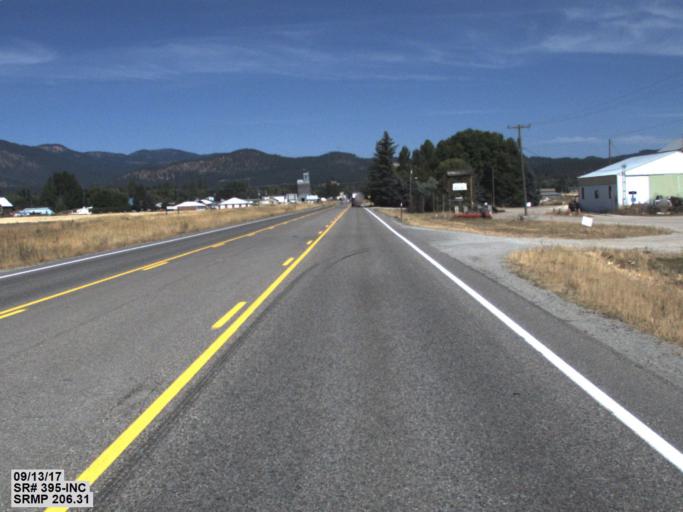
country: US
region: Washington
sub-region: Stevens County
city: Chewelah
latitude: 48.2642
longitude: -117.7153
